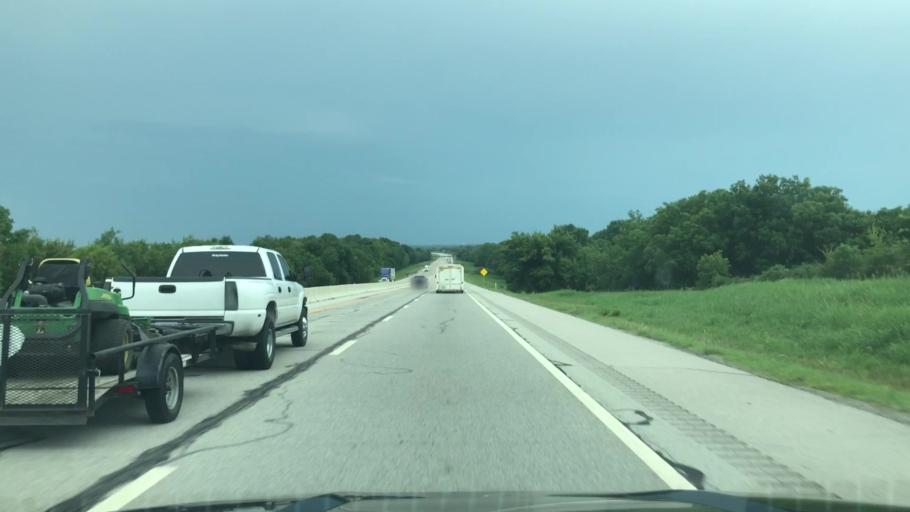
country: US
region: Oklahoma
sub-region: Rogers County
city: Chelsea
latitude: 36.4590
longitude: -95.3523
